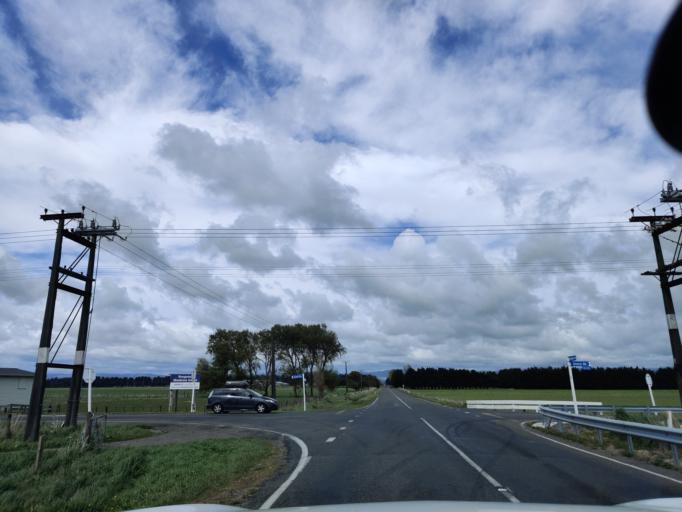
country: NZ
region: Manawatu-Wanganui
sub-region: Palmerston North City
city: Palmerston North
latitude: -40.3342
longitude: 175.5156
